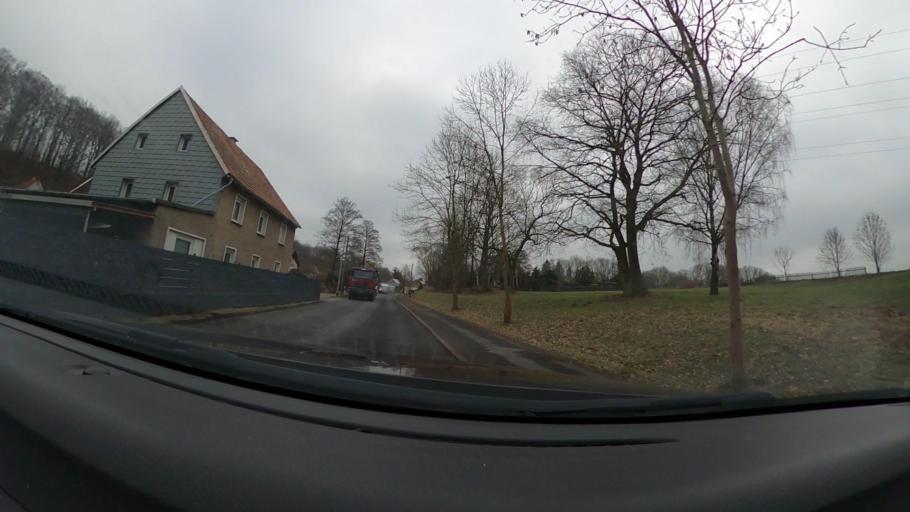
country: DE
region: Saxony
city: Oberschona
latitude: 50.8984
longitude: 13.2513
